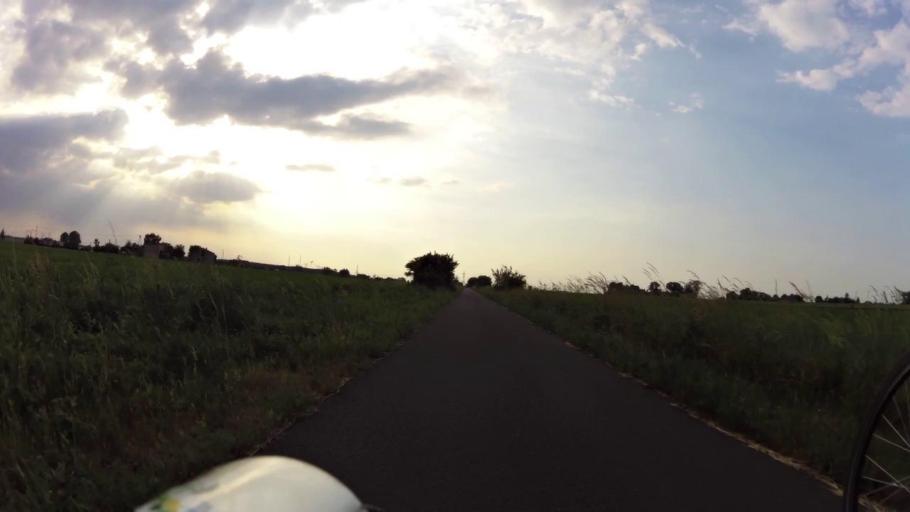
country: PL
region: Kujawsko-Pomorskie
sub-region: Powiat chelminski
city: Unislaw
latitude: 53.1758
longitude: 18.4142
